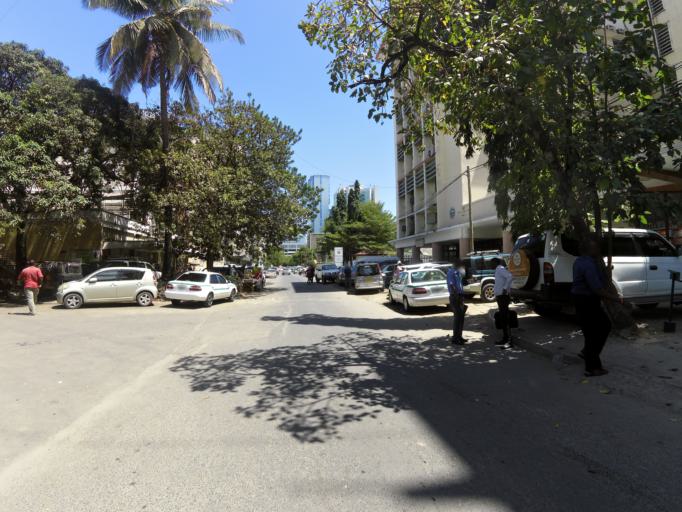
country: TZ
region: Dar es Salaam
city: Dar es Salaam
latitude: -6.8168
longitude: 39.2911
